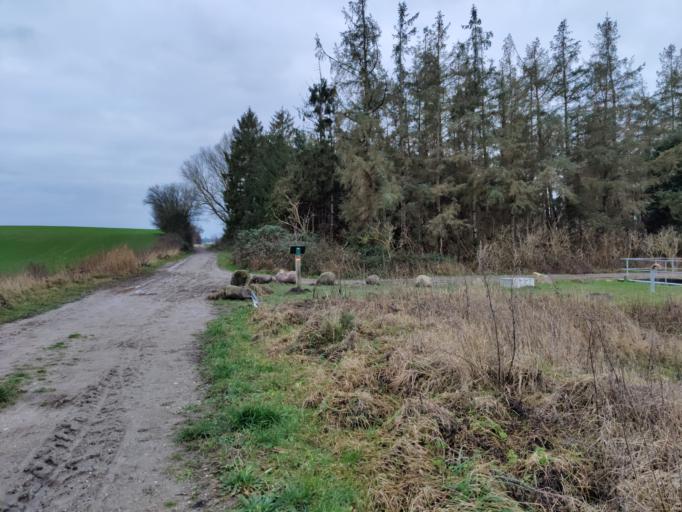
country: DK
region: South Denmark
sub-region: Kerteminde Kommune
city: Kerteminde
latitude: 55.4724
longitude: 10.6546
